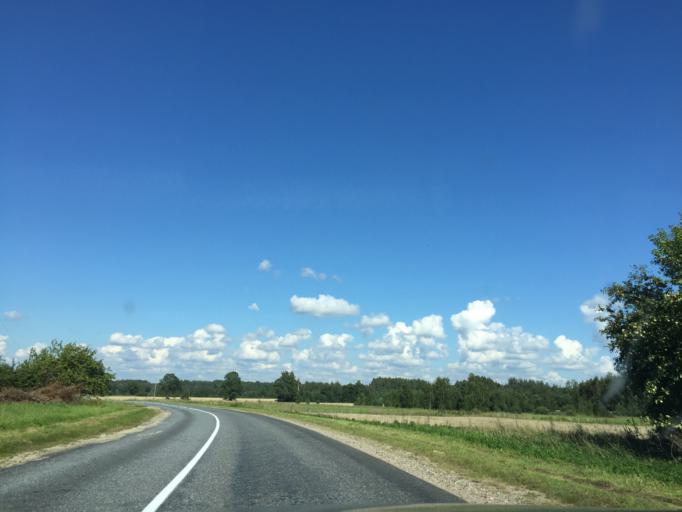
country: LV
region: Limbazu Rajons
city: Limbazi
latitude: 57.4309
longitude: 24.7138
